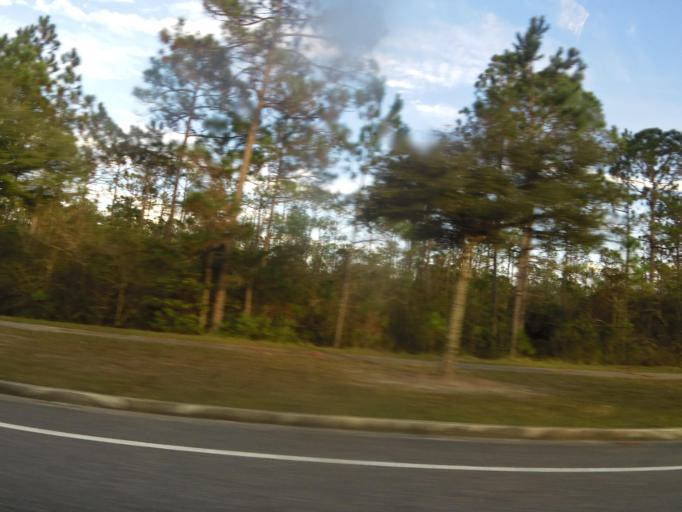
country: US
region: Florida
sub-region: Duval County
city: Baldwin
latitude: 30.2533
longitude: -81.8864
